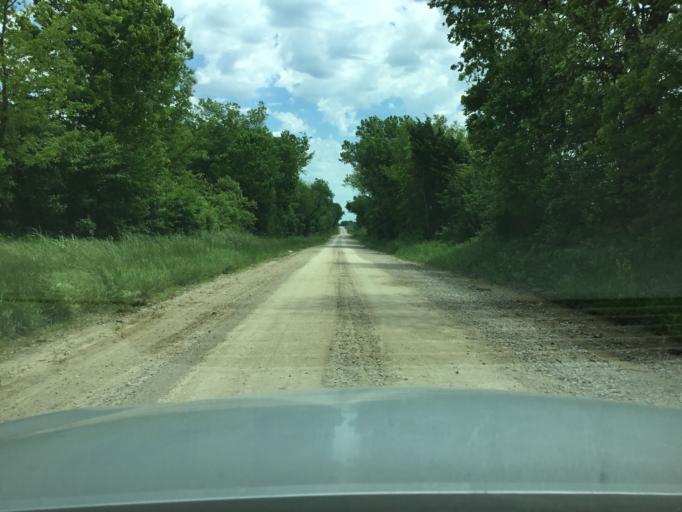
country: US
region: Kansas
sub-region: Montgomery County
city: Independence
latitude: 37.0952
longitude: -95.7943
